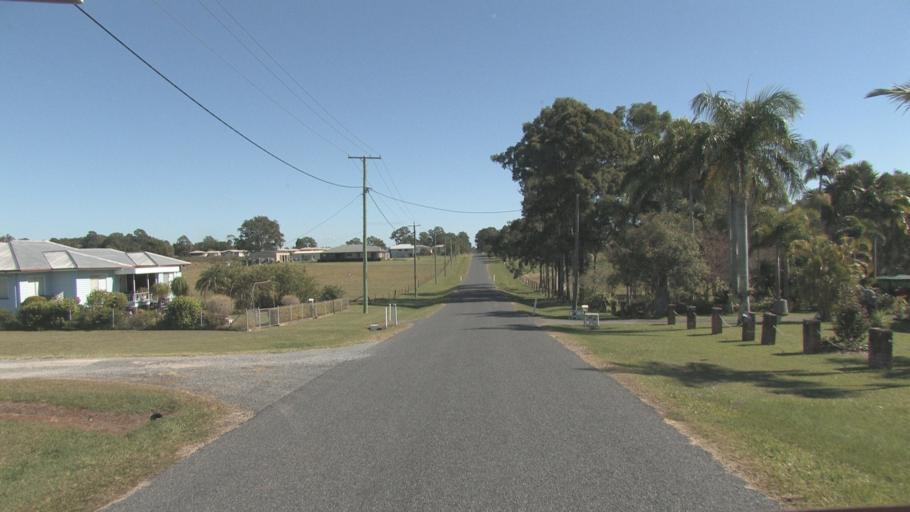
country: AU
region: Queensland
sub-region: Gold Coast
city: Yatala
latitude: -27.6881
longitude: 153.2230
